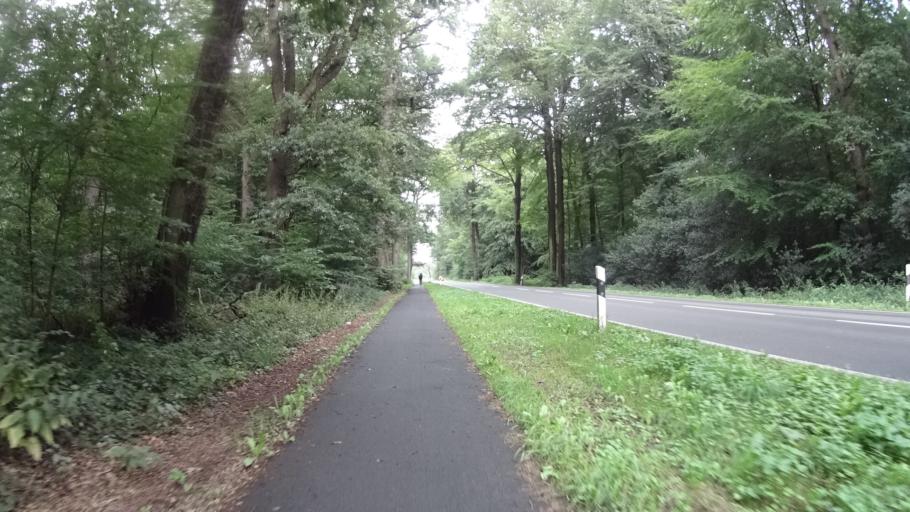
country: DE
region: Lower Saxony
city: Zetel
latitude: 53.3925
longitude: 7.9661
